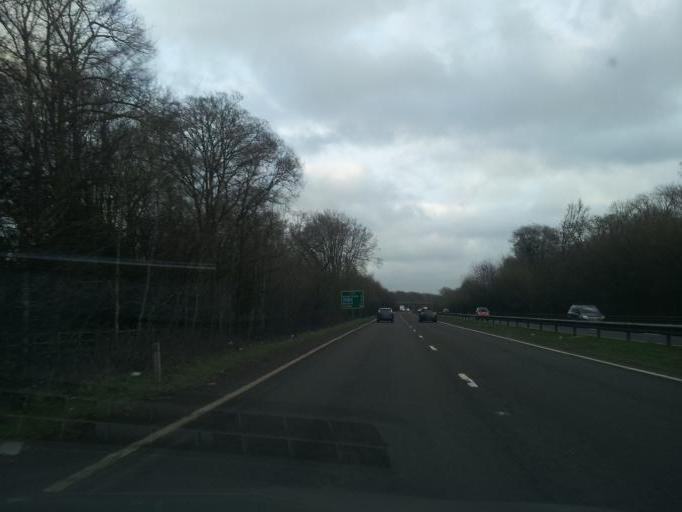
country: GB
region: England
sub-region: Hertfordshire
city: Berkhamsted
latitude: 51.7492
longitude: -0.5640
